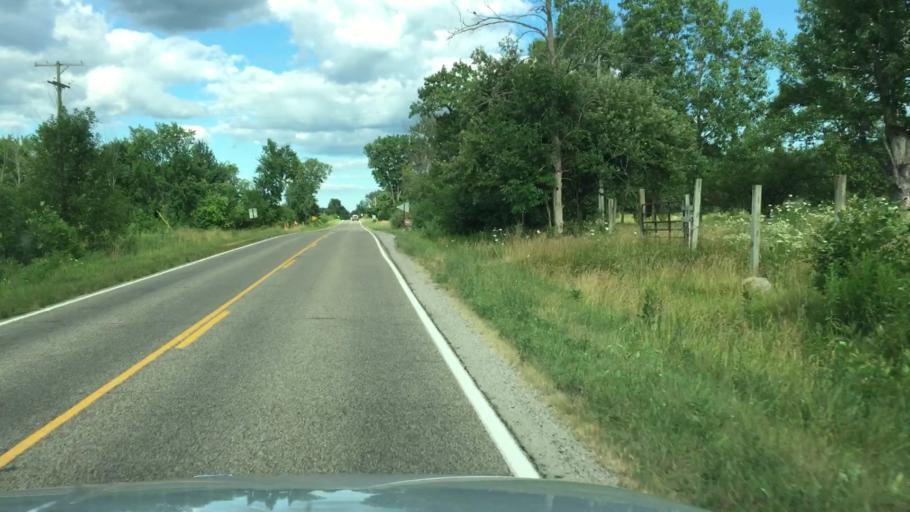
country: US
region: Michigan
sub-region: Saint Clair County
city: Yale
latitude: 43.1286
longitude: -82.8506
